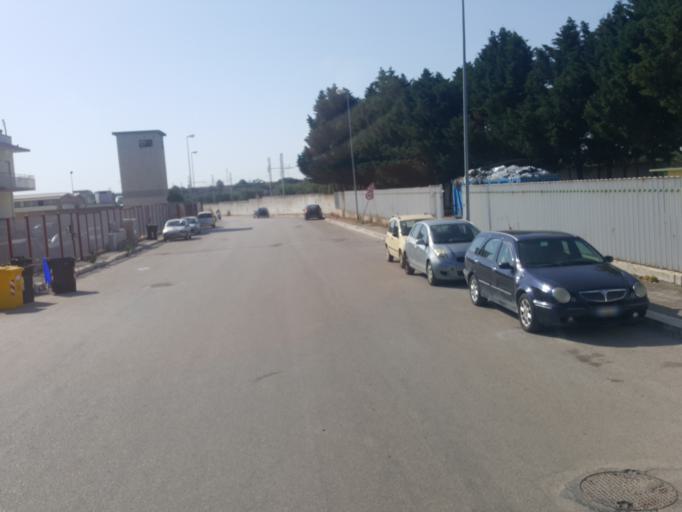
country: IT
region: Apulia
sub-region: Provincia di Barletta - Andria - Trani
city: Barletta
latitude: 41.3083
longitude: 16.3059
